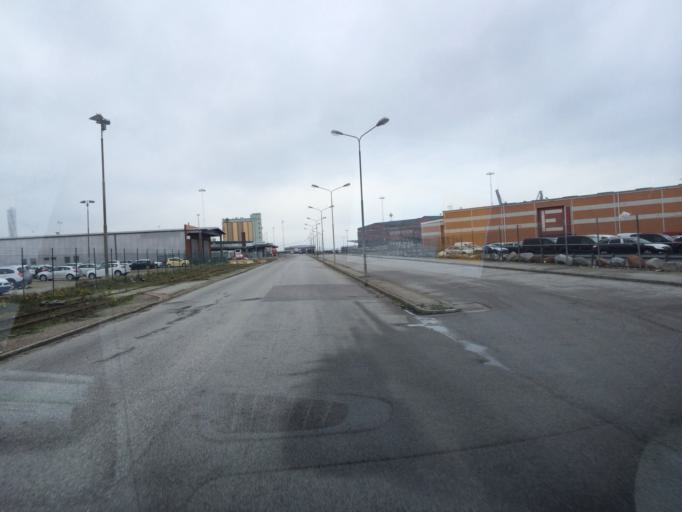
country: SE
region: Skane
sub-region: Malmo
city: Malmoe
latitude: 55.6136
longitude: 13.0110
